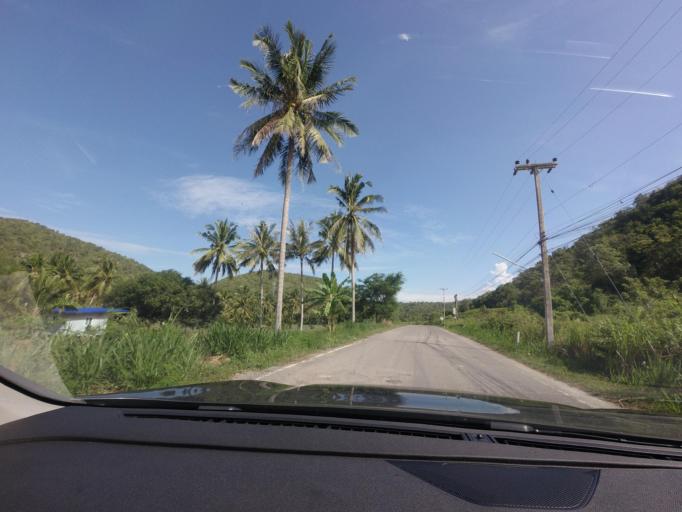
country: TH
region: Prachuap Khiri Khan
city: Pran Buri
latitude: 12.4651
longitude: 99.9456
